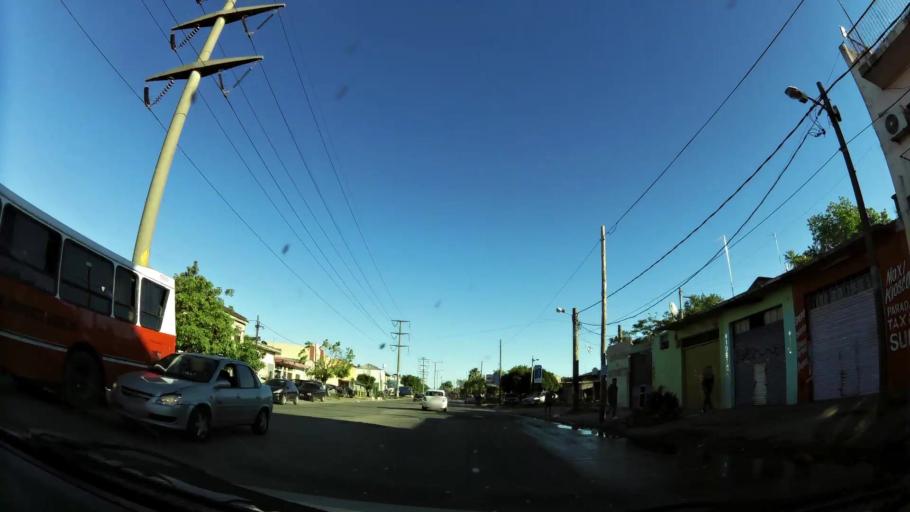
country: AR
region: Buenos Aires
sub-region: Partido de Almirante Brown
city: Adrogue
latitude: -34.7542
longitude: -58.3369
